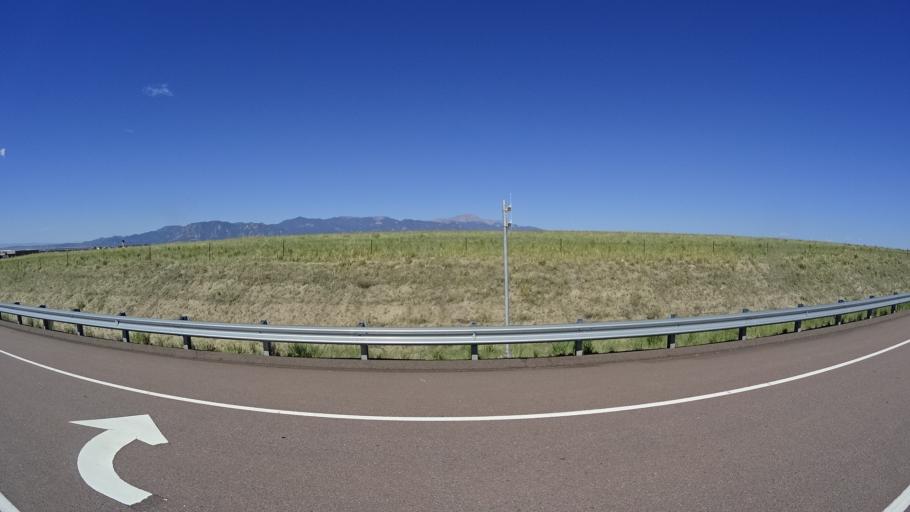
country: US
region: Colorado
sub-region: El Paso County
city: Cimarron Hills
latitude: 38.8288
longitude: -104.6825
